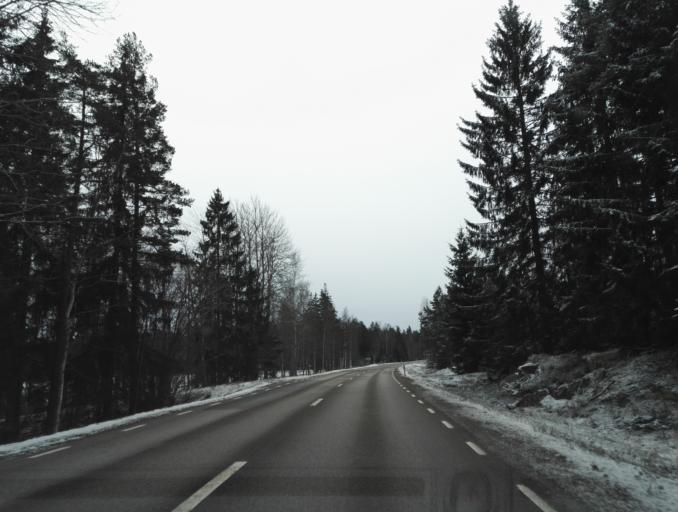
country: SE
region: Kalmar
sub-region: Hultsfreds Kommun
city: Virserum
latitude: 57.2789
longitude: 15.5693
